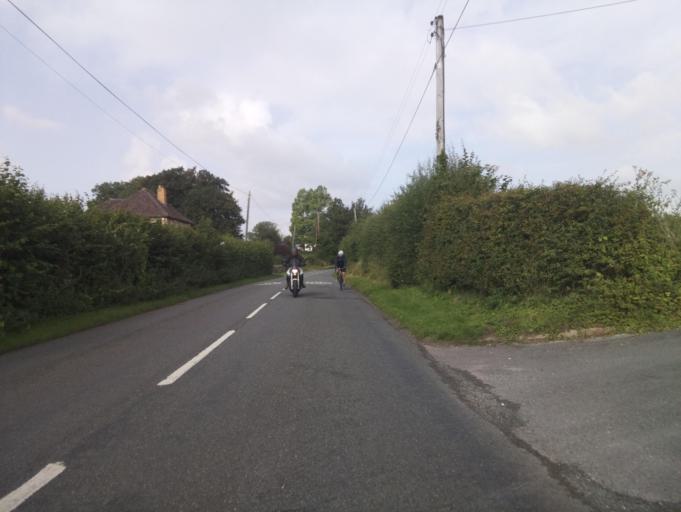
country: GB
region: England
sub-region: Bath and North East Somerset
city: Cameley
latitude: 51.2889
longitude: -2.5855
